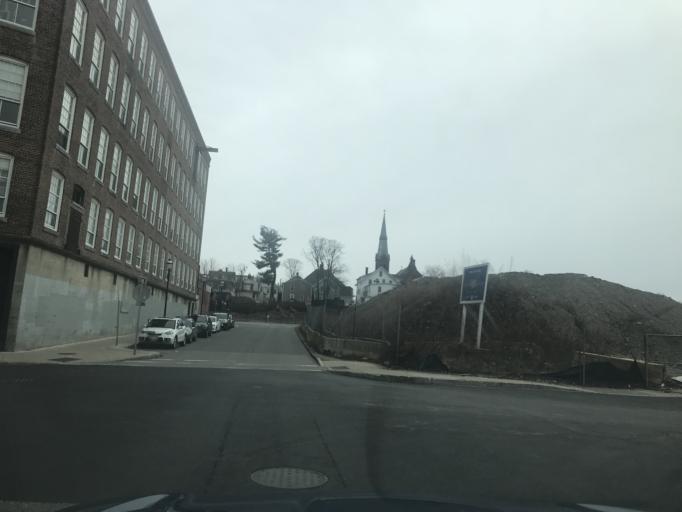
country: US
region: Massachusetts
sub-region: Middlesex County
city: Lowell
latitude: 42.6411
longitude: -71.3134
